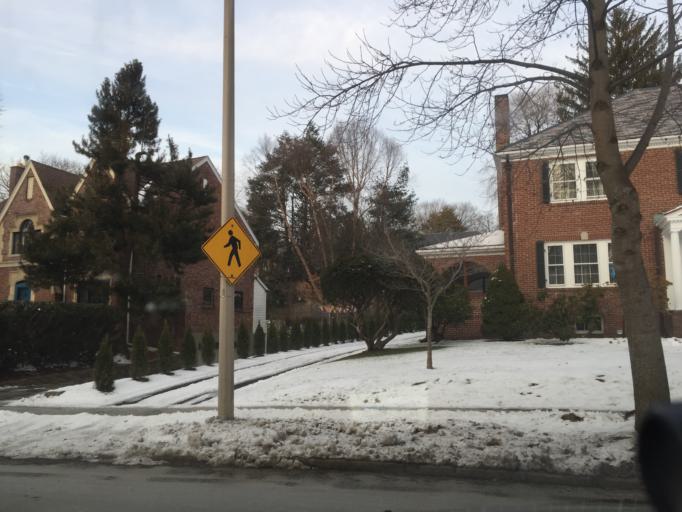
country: US
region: Massachusetts
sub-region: Norfolk County
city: Brookline
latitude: 42.3297
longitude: -71.1508
